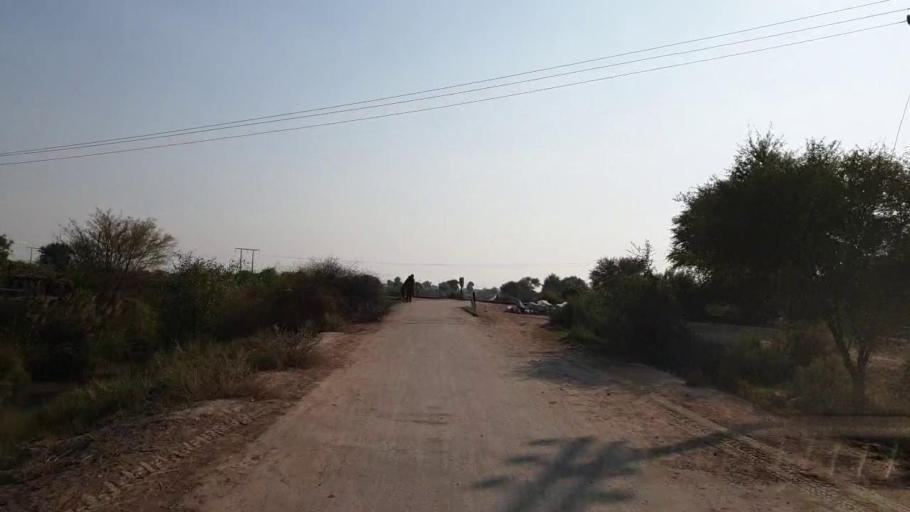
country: PK
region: Sindh
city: Sehwan
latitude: 26.4468
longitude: 67.8145
